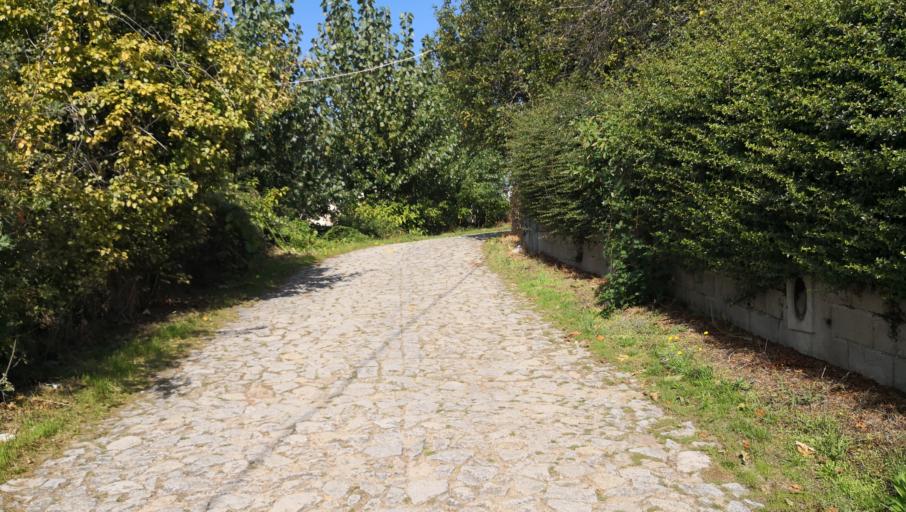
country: PT
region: Vila Real
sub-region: Vila Real
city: Vila Real
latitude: 41.3077
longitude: -7.7311
